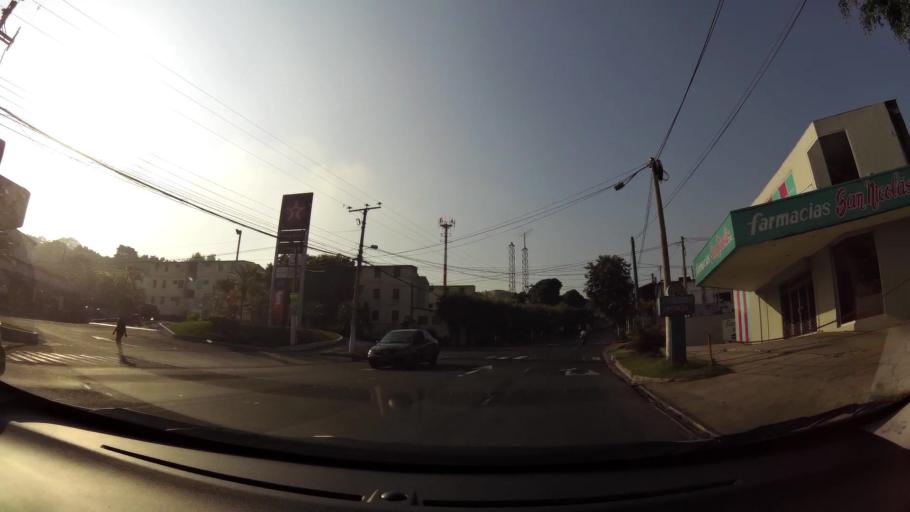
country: SV
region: La Libertad
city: Antiguo Cuscatlan
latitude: 13.6780
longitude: -89.2259
